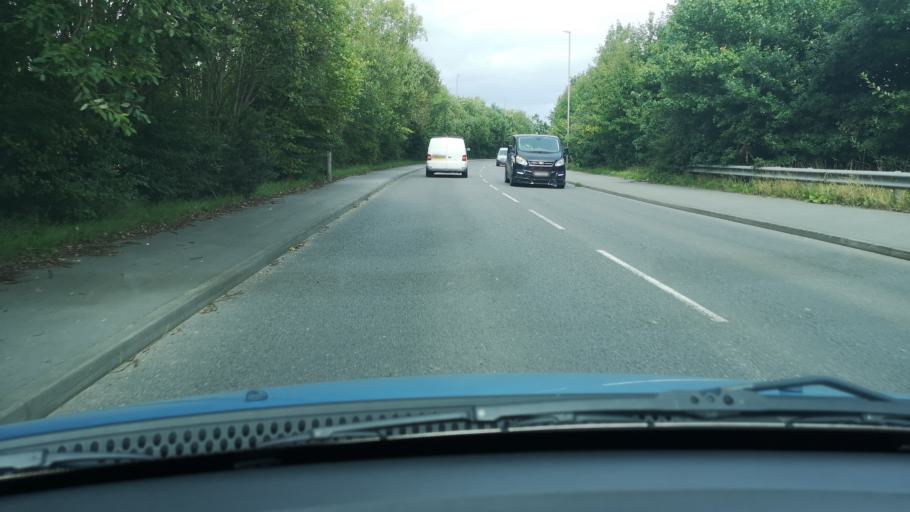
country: GB
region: England
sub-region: Barnsley
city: Shafton
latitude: 53.5915
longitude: -1.3986
